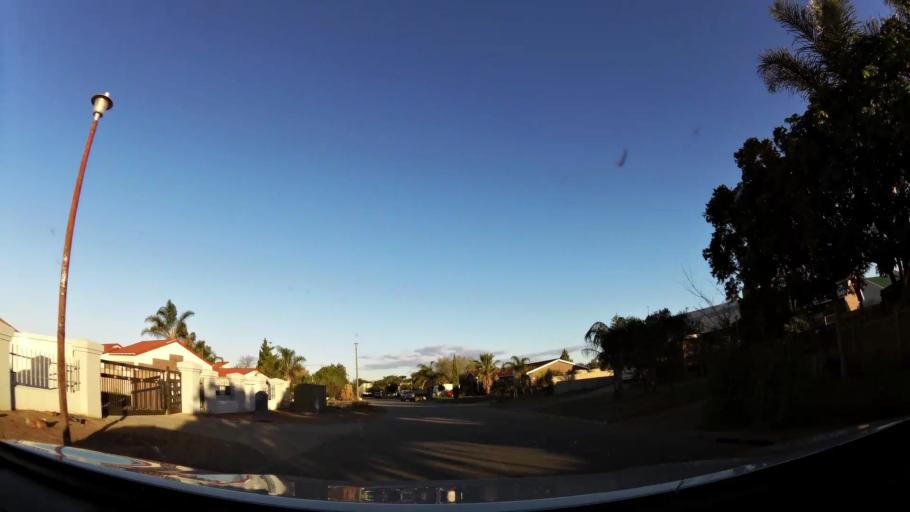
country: ZA
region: Western Cape
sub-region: Eden District Municipality
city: Riversdale
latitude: -34.0839
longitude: 21.2425
